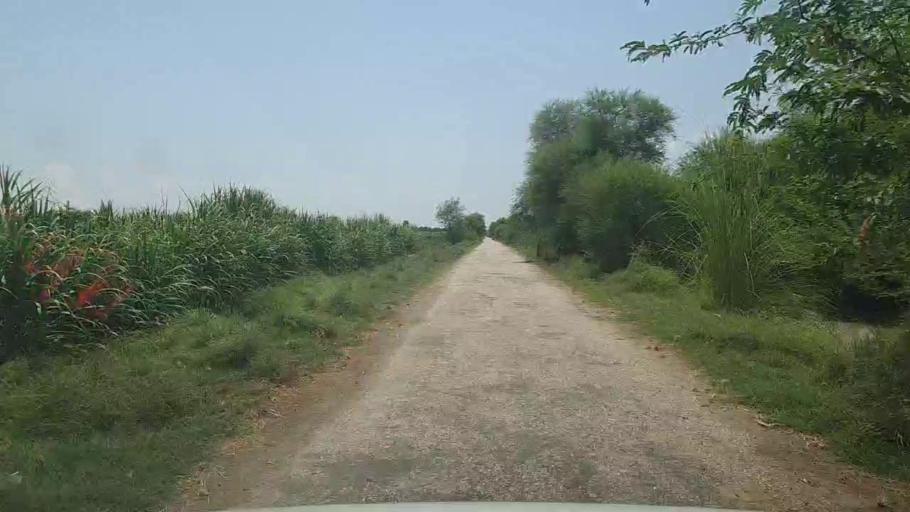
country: PK
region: Sindh
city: Ubauro
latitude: 28.1619
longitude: 69.7458
